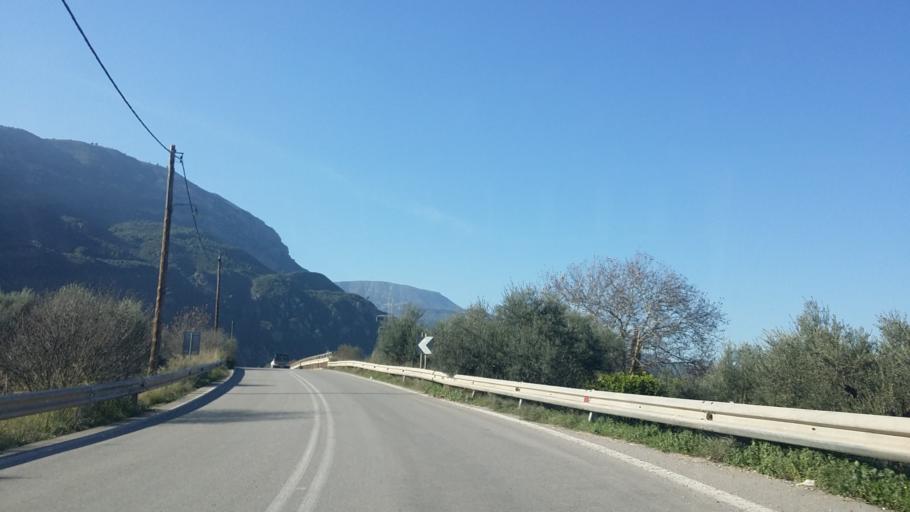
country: GR
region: West Greece
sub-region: Nomos Achaias
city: Temeni
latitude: 38.1876
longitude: 22.1915
